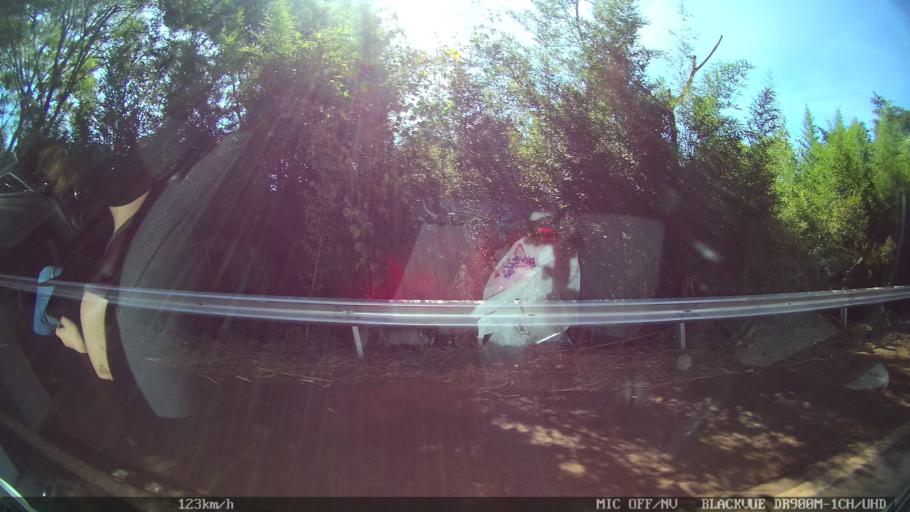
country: BR
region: Sao Paulo
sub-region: Sao Joaquim Da Barra
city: Sao Joaquim da Barra
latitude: -20.5419
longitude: -47.8009
